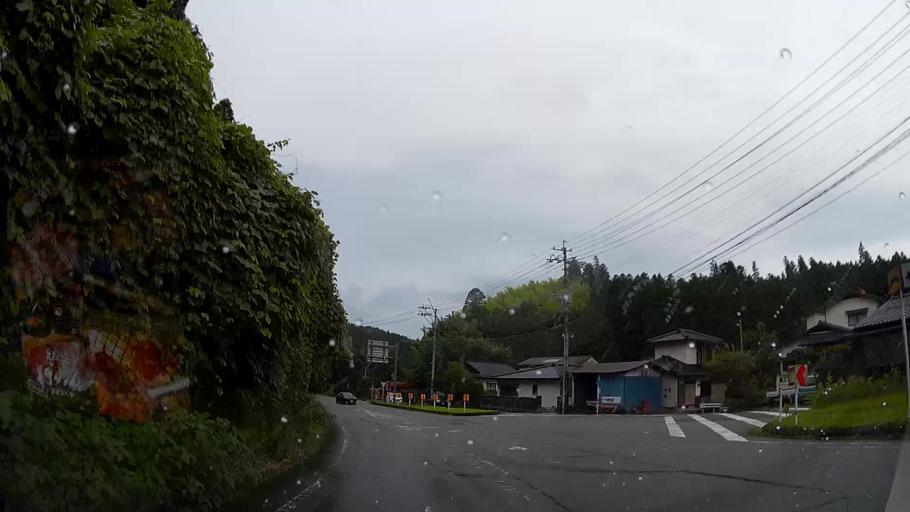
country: JP
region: Oita
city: Tsukawaki
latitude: 33.1381
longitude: 131.0629
